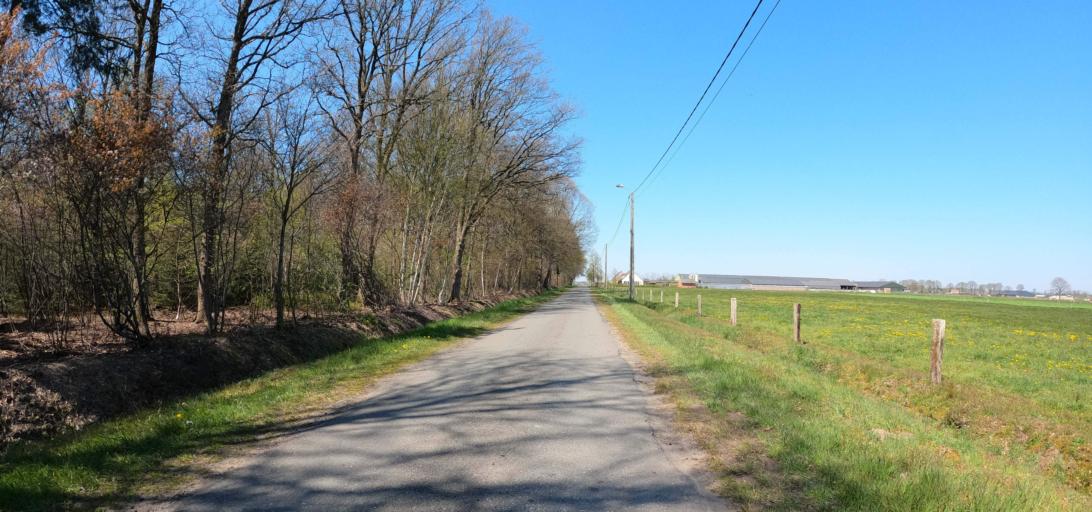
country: BE
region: Flanders
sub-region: Provincie Antwerpen
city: Oostmalle
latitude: 51.3093
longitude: 4.7574
